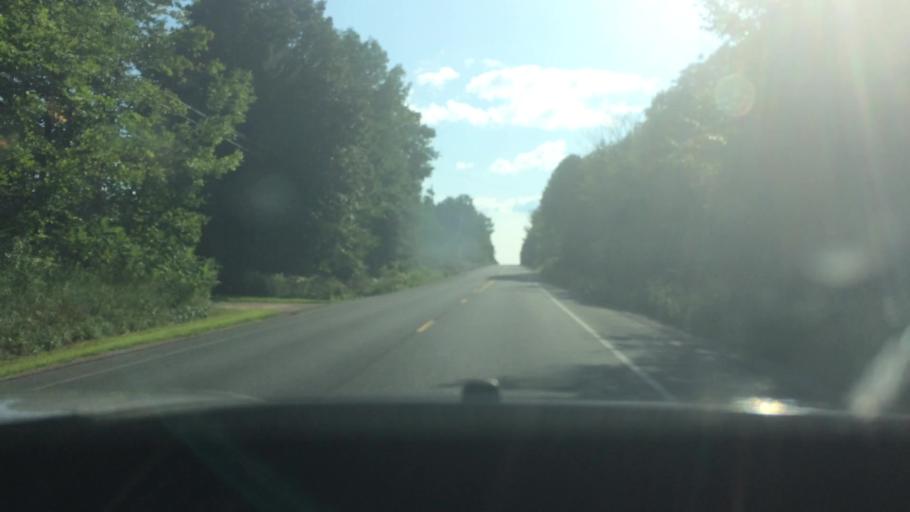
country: US
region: New York
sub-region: Franklin County
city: Malone
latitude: 44.7598
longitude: -74.5405
